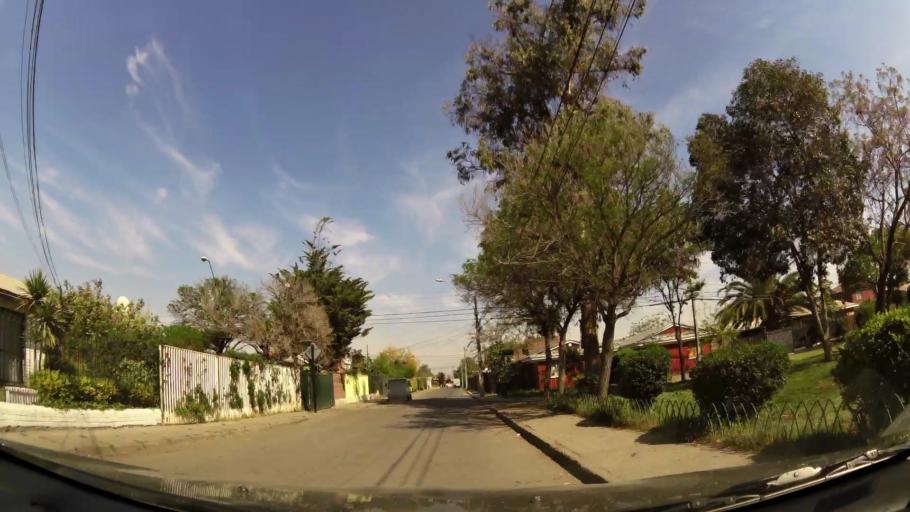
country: CL
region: Santiago Metropolitan
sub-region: Provincia de Cordillera
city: Puente Alto
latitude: -33.5704
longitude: -70.5871
